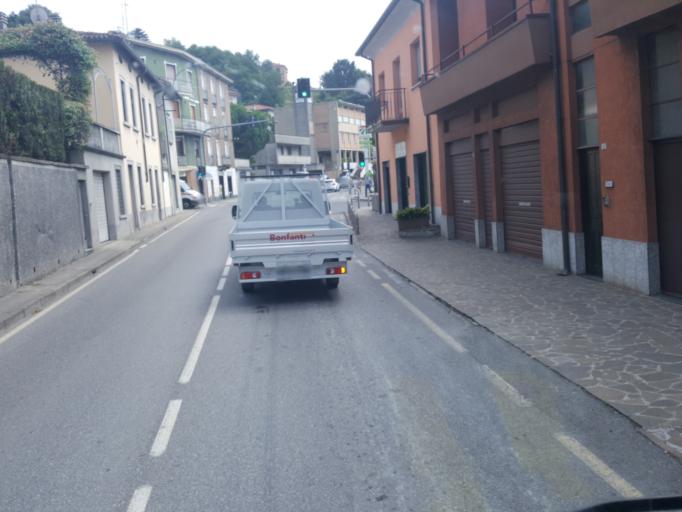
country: IT
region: Lombardy
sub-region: Provincia di Lecco
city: Vercurago
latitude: 45.8128
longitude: 9.4240
